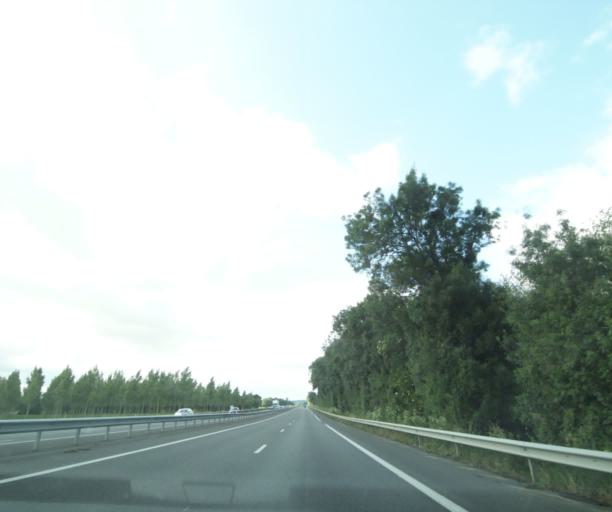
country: FR
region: Pays de la Loire
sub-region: Departement de Maine-et-Loire
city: Vivy
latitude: 47.3011
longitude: -0.0380
